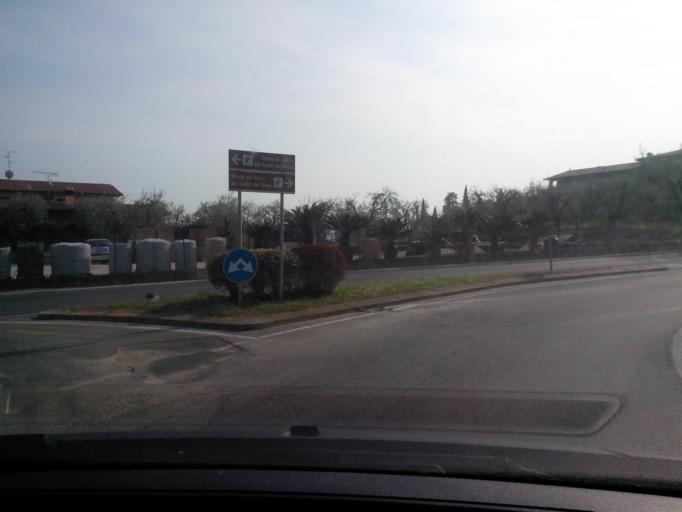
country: IT
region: Lombardy
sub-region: Provincia di Brescia
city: San Felice del Benaco
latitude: 45.5944
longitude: 10.5554
